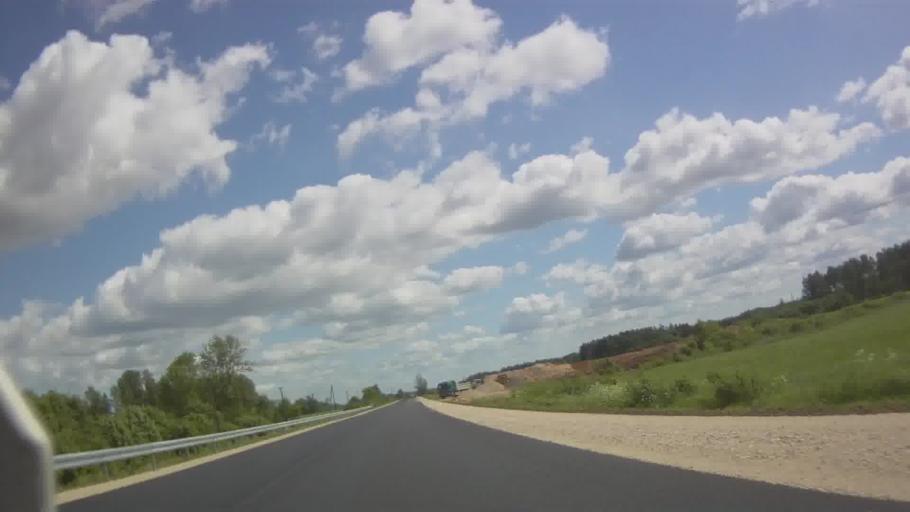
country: LV
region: Vilanu
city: Vilani
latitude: 56.5646
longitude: 26.9628
